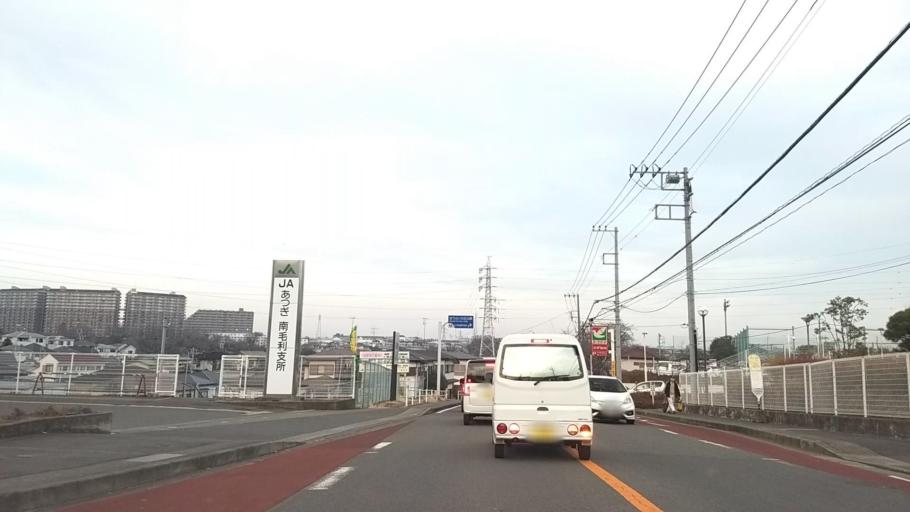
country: JP
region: Kanagawa
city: Atsugi
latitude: 35.4363
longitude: 139.3385
